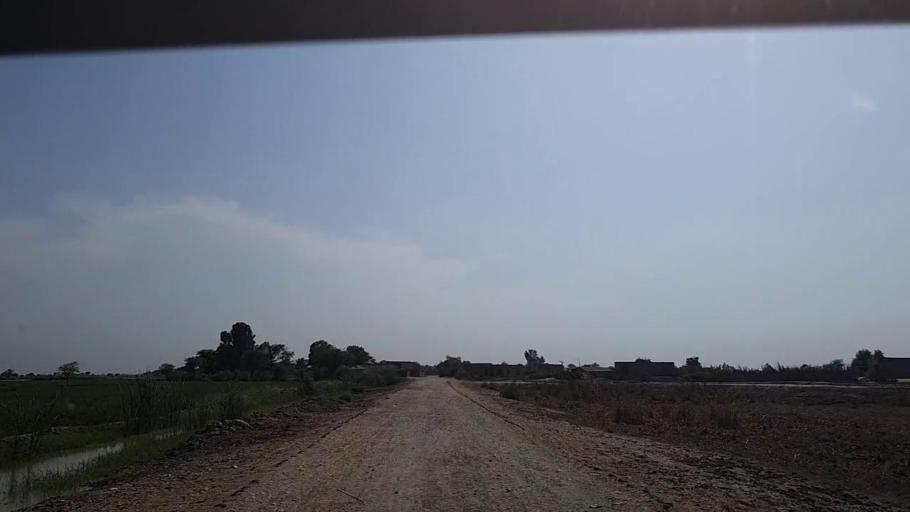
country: PK
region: Sindh
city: Khanpur
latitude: 27.8510
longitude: 69.3589
